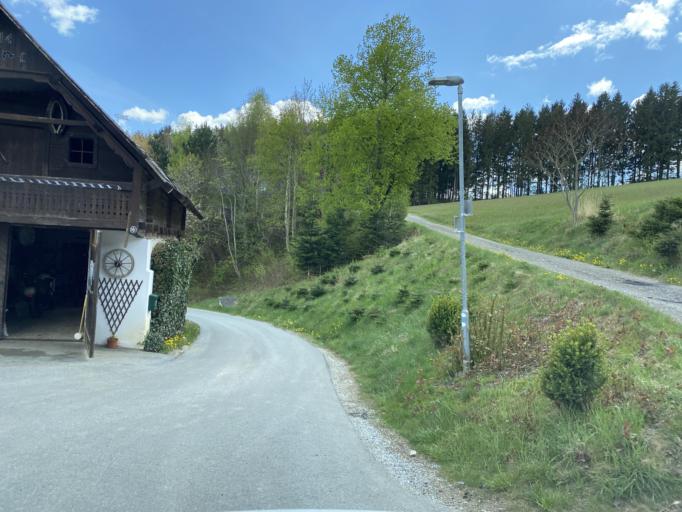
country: AT
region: Styria
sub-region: Politischer Bezirk Weiz
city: Birkfeld
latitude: 47.3554
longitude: 15.6847
